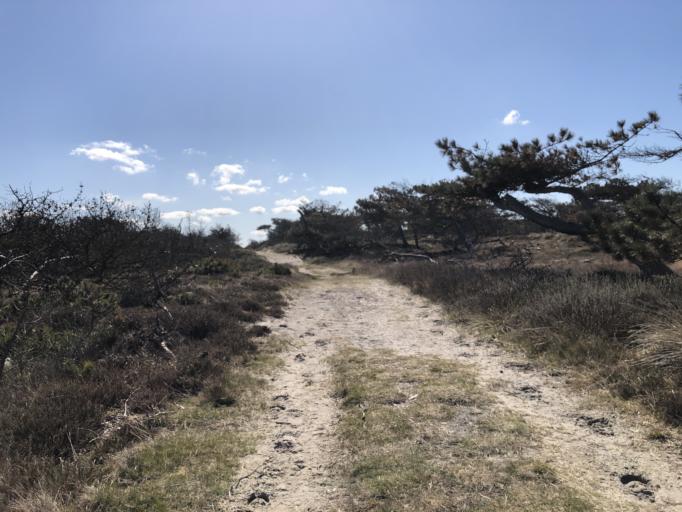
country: DK
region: Central Jutland
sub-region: Holstebro Kommune
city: Ulfborg
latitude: 56.3055
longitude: 8.1300
